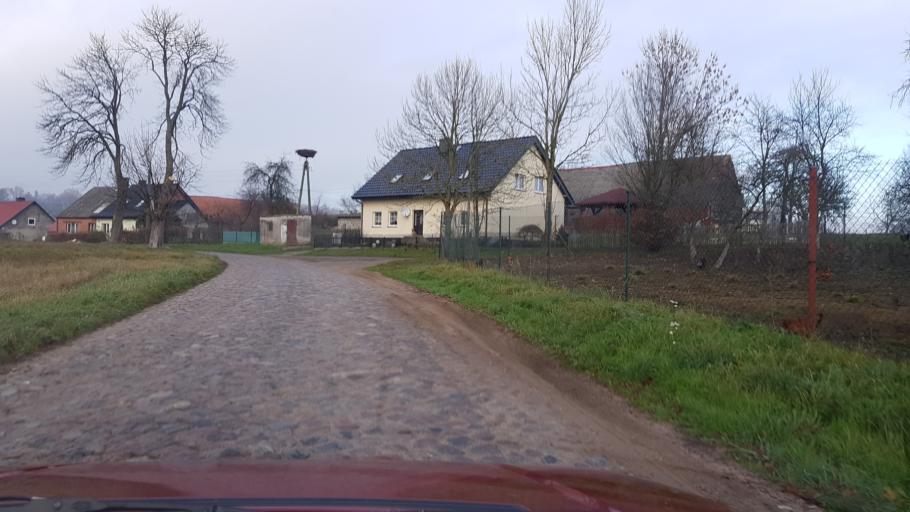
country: PL
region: West Pomeranian Voivodeship
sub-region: Powiat bialogardzki
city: Tychowo
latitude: 53.9784
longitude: 16.3152
